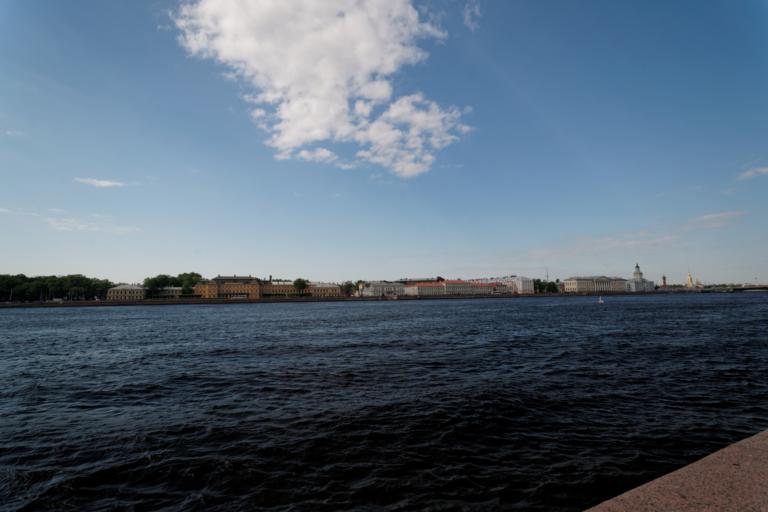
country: RU
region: St.-Petersburg
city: Saint Petersburg
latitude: 59.9361
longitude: 30.2994
